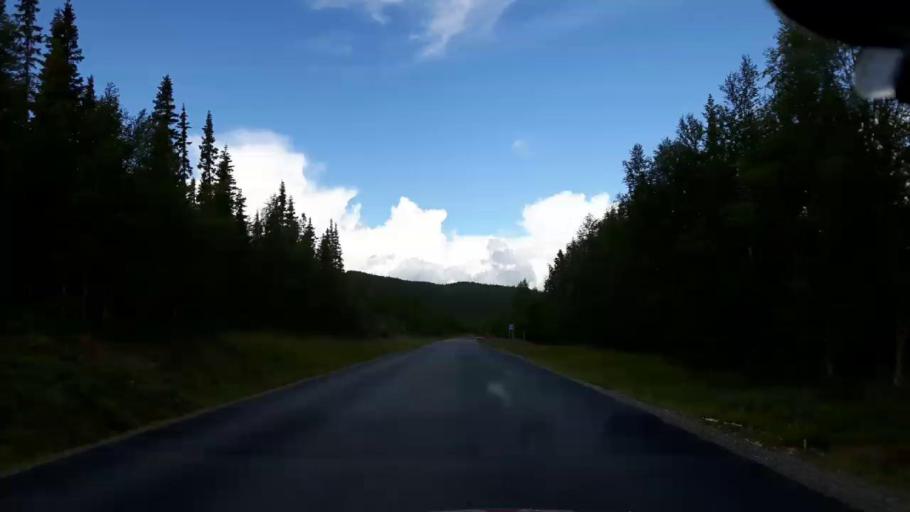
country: SE
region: Vaesterbotten
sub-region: Vilhelmina Kommun
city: Sjoberg
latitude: 65.0090
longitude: 15.1810
